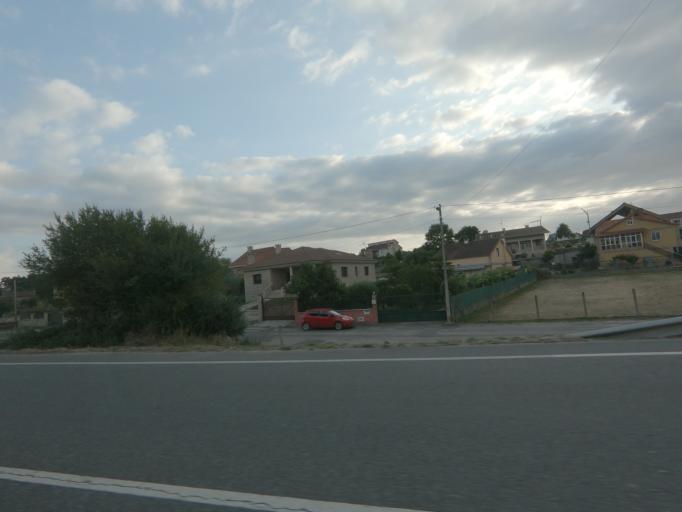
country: ES
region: Galicia
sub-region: Provincia de Ourense
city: Taboadela
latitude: 42.2828
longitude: -7.8399
